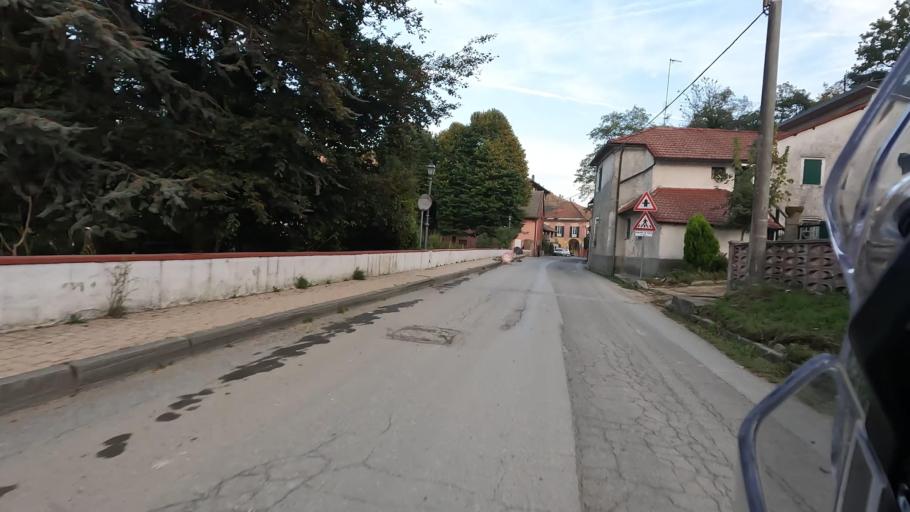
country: IT
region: Liguria
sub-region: Provincia di Savona
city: Pontinvrea
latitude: 44.4458
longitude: 8.4330
